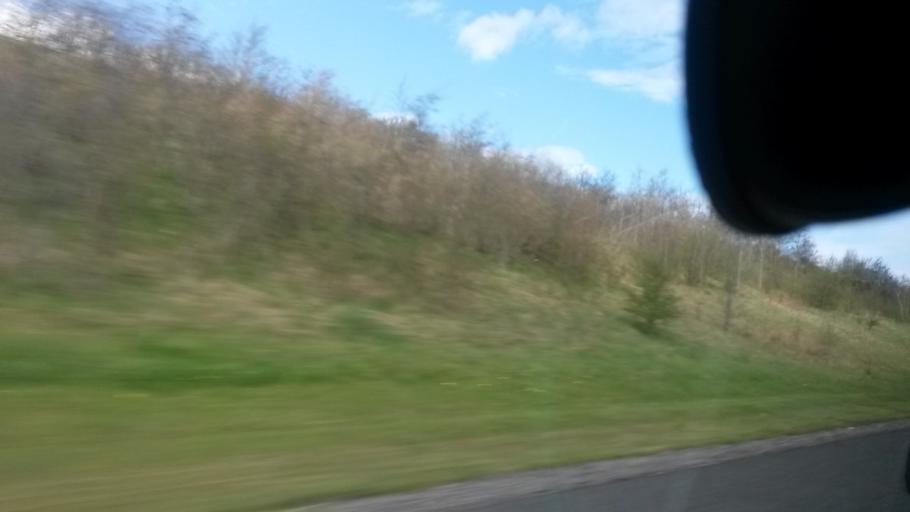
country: IE
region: Leinster
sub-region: Kildare
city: Monasterevin
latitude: 53.1205
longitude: -7.0423
